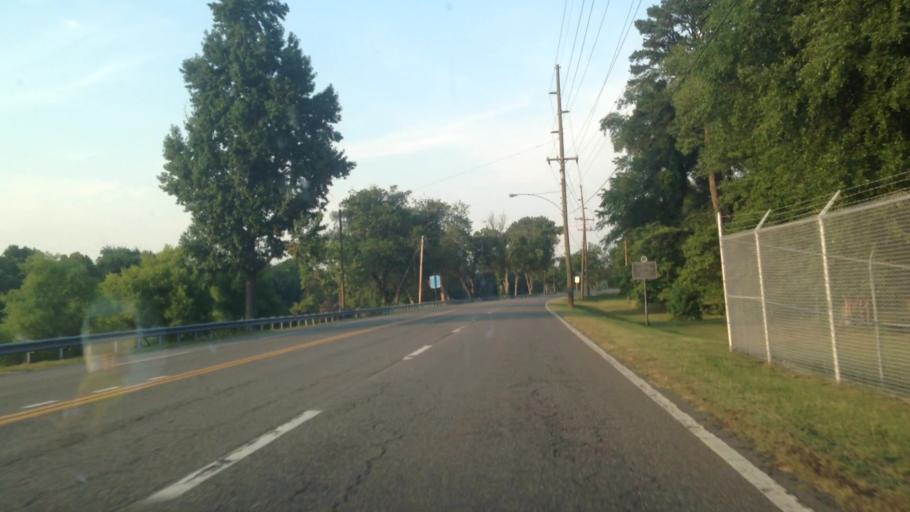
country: US
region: Virginia
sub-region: City of Danville
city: Danville
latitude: 36.5798
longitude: -79.4279
